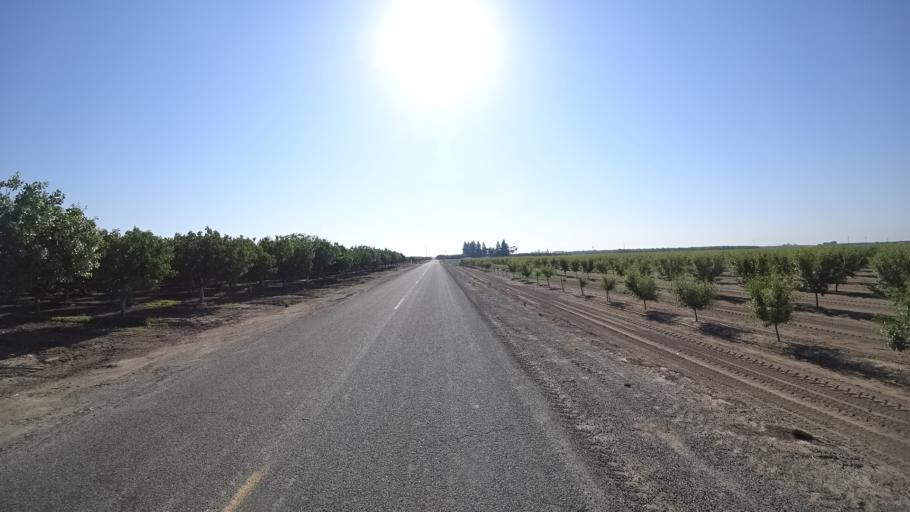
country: US
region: California
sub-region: Kings County
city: Lucerne
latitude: 36.3862
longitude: -119.6951
